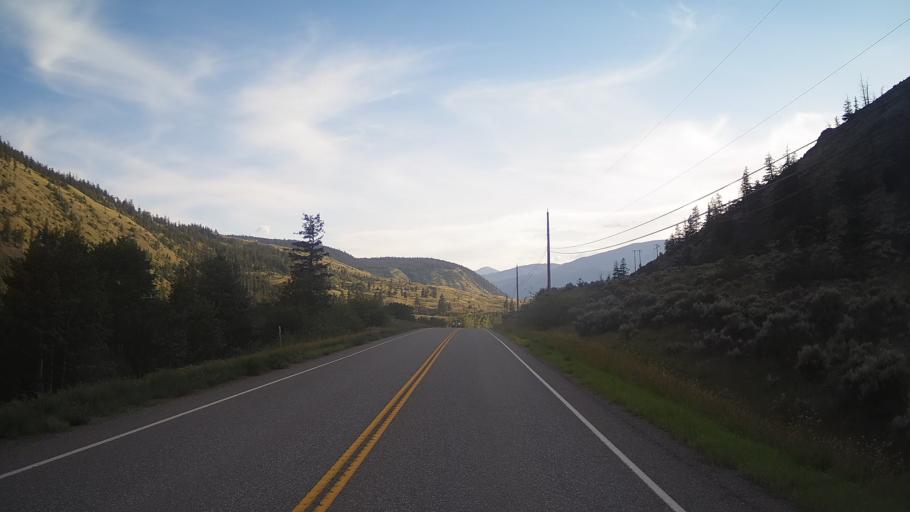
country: CA
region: British Columbia
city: Lillooet
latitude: 50.8908
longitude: -121.8072
